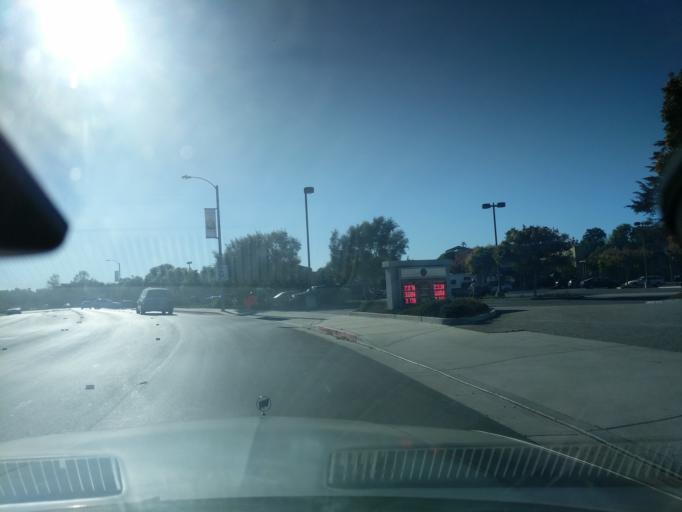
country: US
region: California
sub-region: Santa Barbara County
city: Goleta
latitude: 34.4417
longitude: -119.8310
